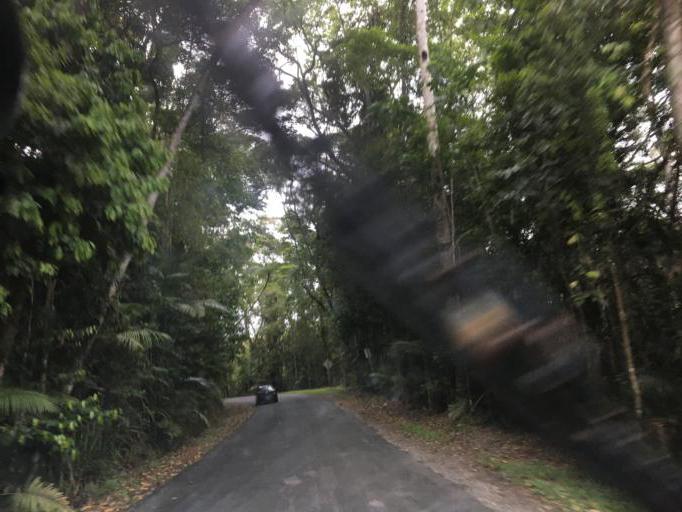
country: AU
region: Queensland
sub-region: Tablelands
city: Kuranda
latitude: -16.8346
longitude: 145.6352
